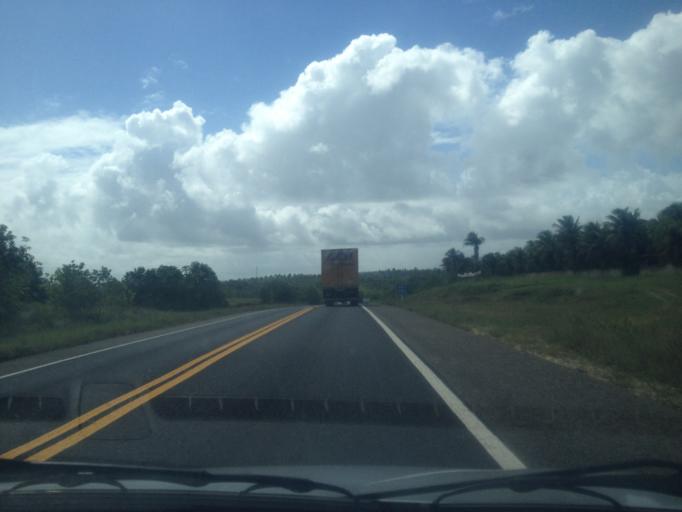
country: BR
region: Sergipe
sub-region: Indiaroba
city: Indiaroba
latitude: -11.6355
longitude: -37.5394
